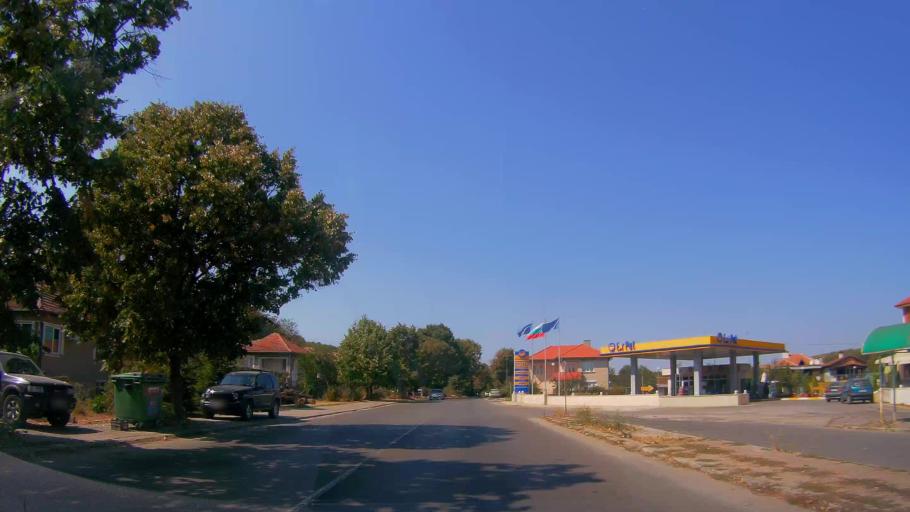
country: BG
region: Razgrad
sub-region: Obshtina Tsar Kaloyan
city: Tsar Kaloyan
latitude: 43.6091
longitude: 26.2362
